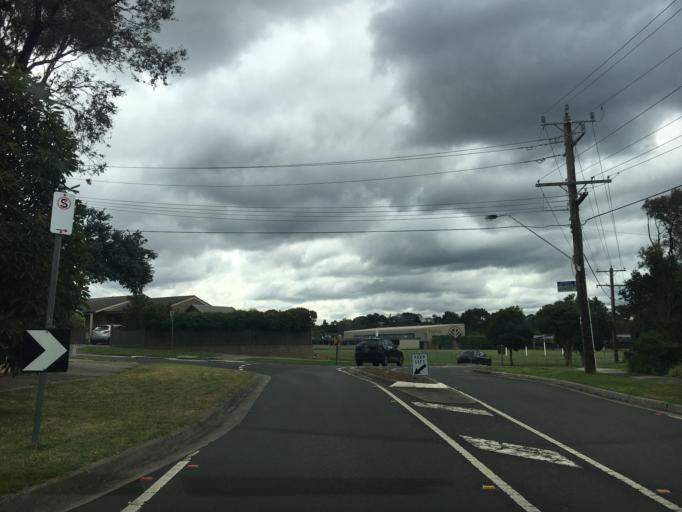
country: AU
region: Victoria
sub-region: Whitehorse
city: Vermont South
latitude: -37.8682
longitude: 145.1771
